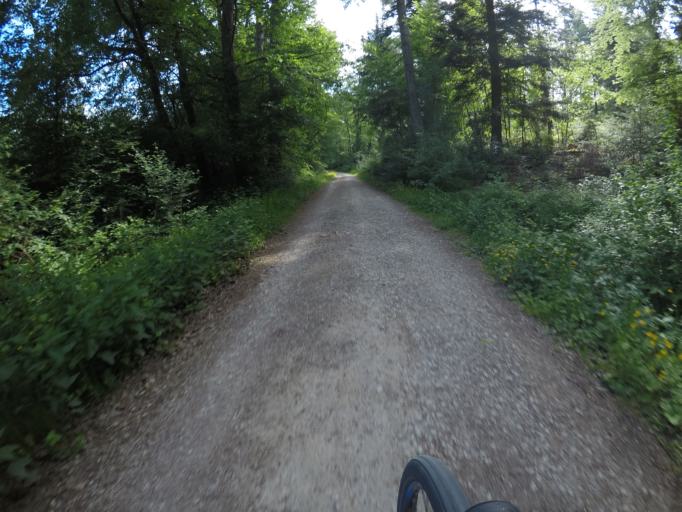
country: DE
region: Baden-Wuerttemberg
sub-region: Regierungsbezirk Stuttgart
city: Neuhausen auf den Fildern
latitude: 48.6798
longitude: 9.3024
